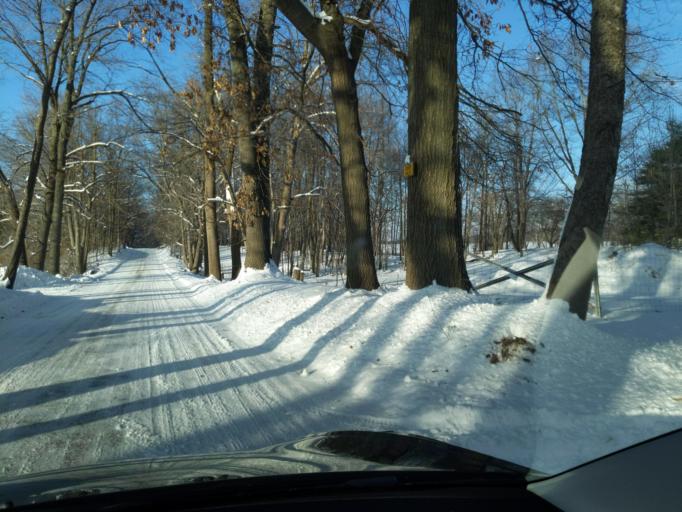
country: US
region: Michigan
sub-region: Ingham County
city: Stockbridge
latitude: 42.4502
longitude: -84.1036
